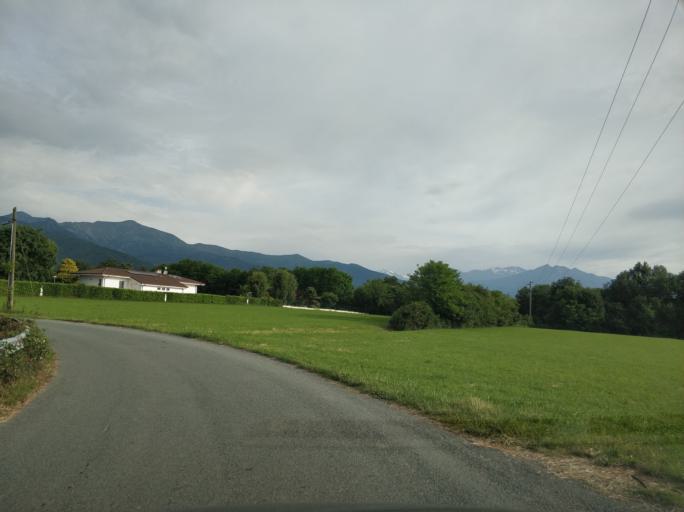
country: IT
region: Piedmont
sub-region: Provincia di Torino
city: Barbania
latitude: 45.2922
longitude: 7.6227
